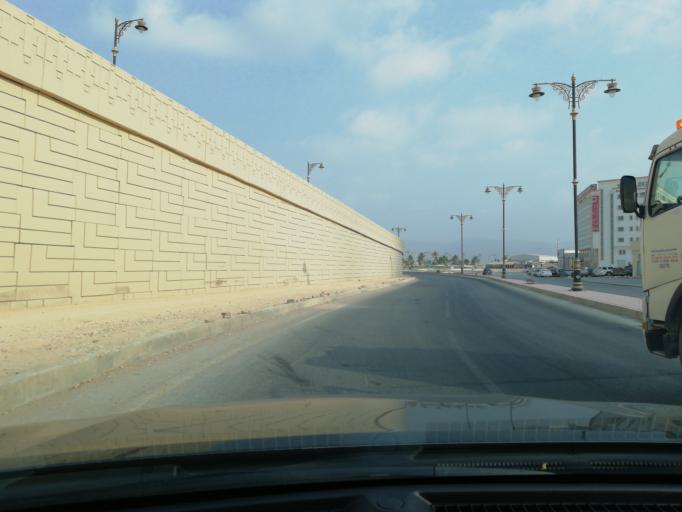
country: OM
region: Zufar
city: Salalah
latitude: 17.0184
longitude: 54.0593
